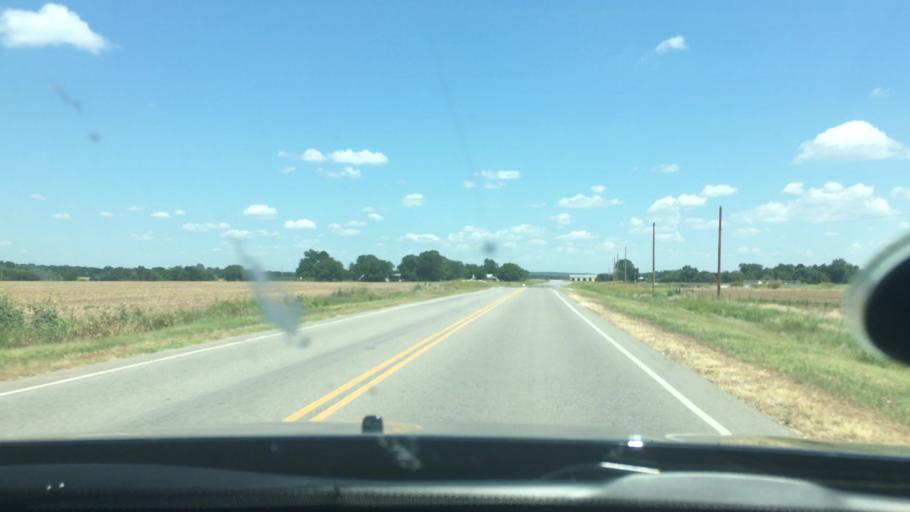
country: US
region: Oklahoma
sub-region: Carter County
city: Dickson
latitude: 34.2265
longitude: -96.9770
